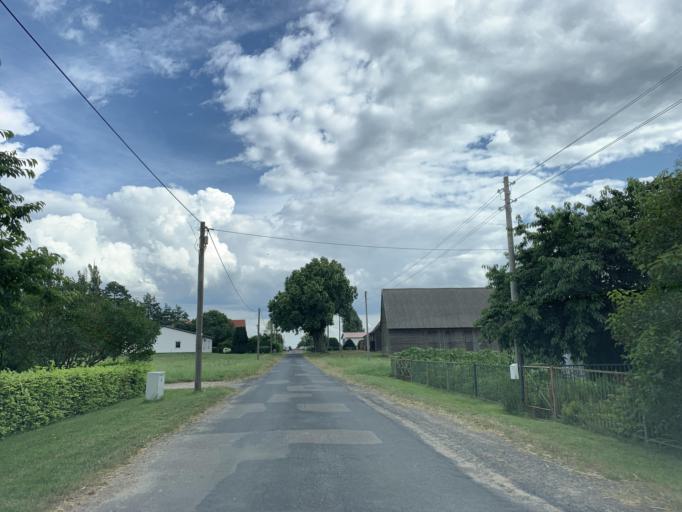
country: DE
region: Mecklenburg-Vorpommern
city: Blankensee
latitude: 53.3757
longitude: 13.2860
